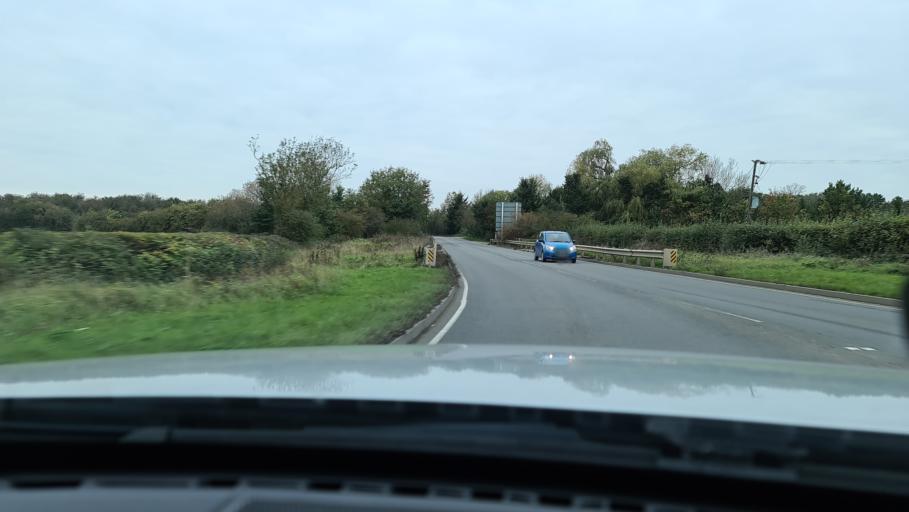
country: GB
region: England
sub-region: Buckinghamshire
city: Waddesdon
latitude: 51.8563
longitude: -0.9750
